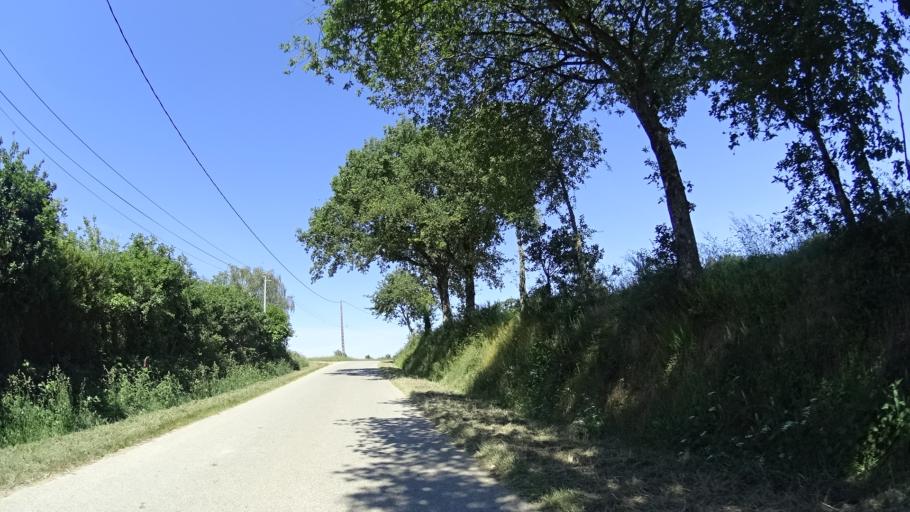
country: FR
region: Brittany
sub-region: Departement d'Ille-et-Vilaine
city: Messac
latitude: 47.7932
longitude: -1.8124
